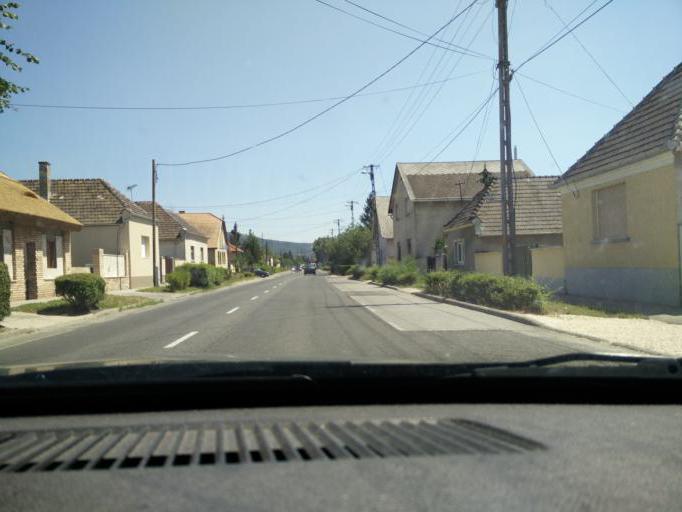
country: HU
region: Komarom-Esztergom
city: Vertesszolos
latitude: 47.6215
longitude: 18.3741
